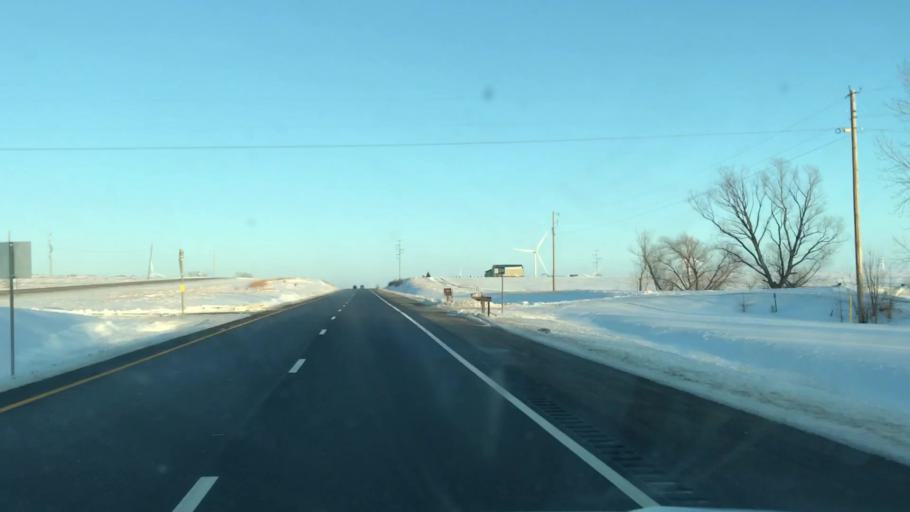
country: US
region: Missouri
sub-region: DeKalb County
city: Maysville
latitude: 39.7618
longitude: -94.4521
